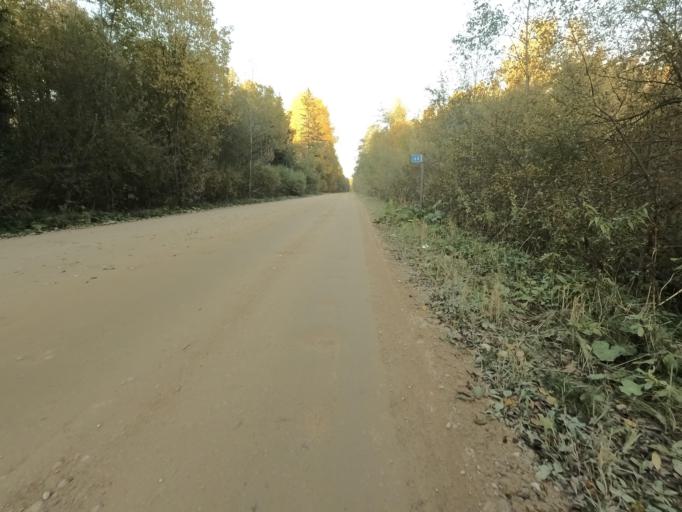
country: RU
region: Leningrad
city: Lyuban'
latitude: 58.9866
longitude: 31.0997
